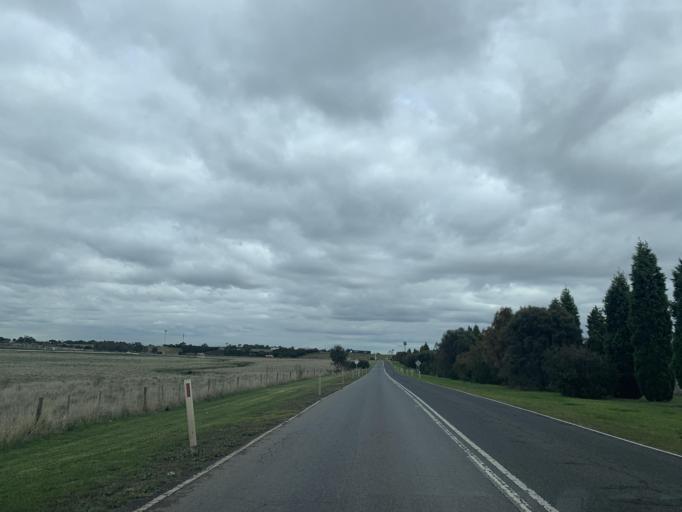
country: AU
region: Victoria
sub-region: Hume
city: Craigieburn
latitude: -37.5976
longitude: 144.9736
